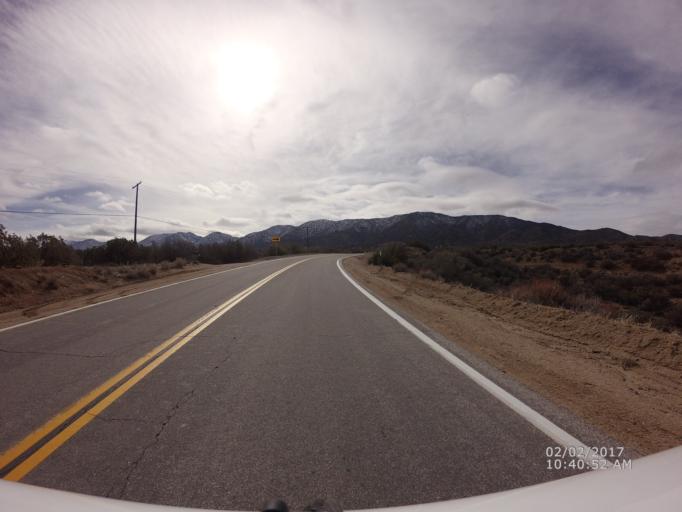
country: US
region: California
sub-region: Los Angeles County
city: Littlerock
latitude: 34.4590
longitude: -117.9346
